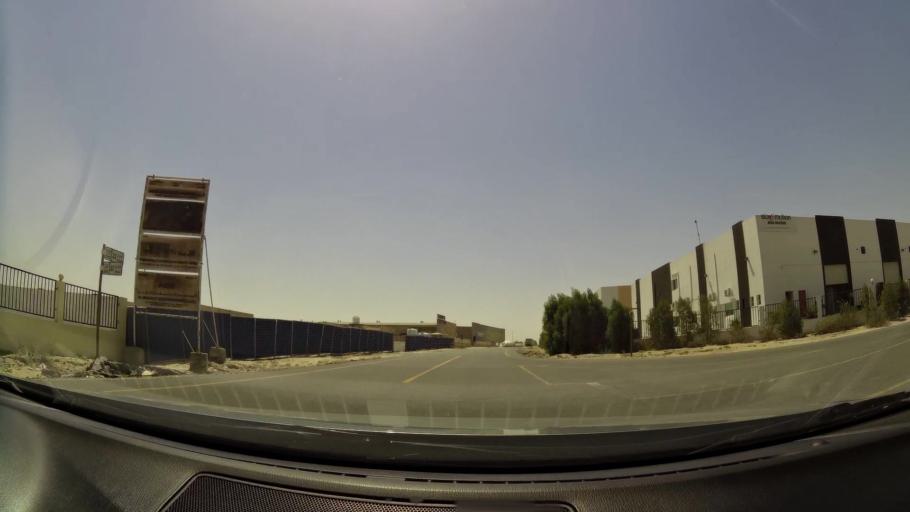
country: AE
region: Dubai
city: Dubai
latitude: 24.9831
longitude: 55.2094
